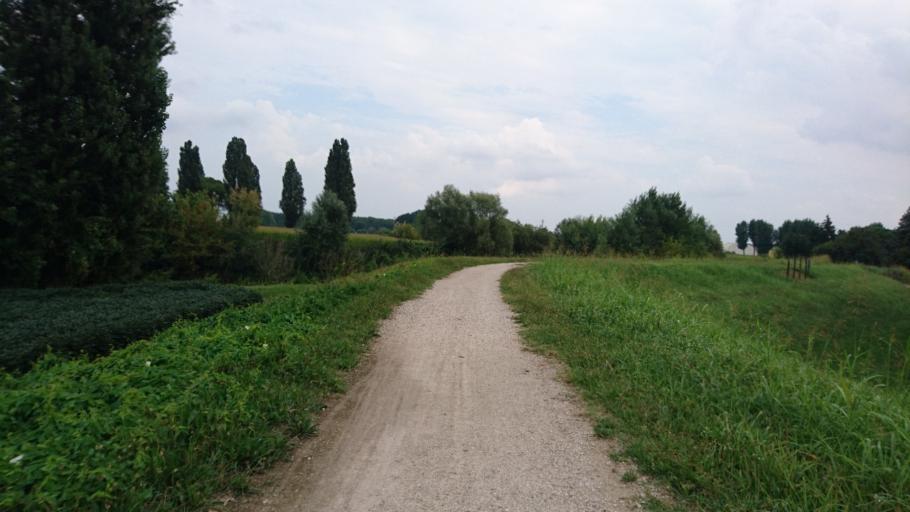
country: IT
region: Veneto
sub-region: Provincia di Padova
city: Saccolongo
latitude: 45.4086
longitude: 11.7427
